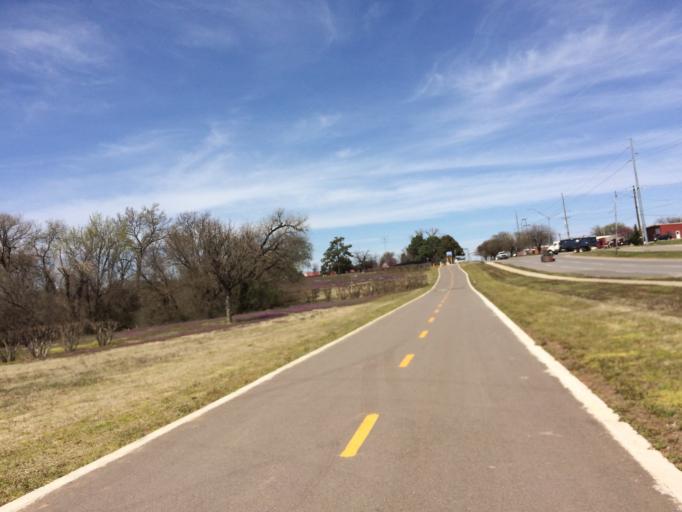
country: US
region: Oklahoma
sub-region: Oklahoma County
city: Oklahoma City
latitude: 35.4749
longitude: -97.5659
